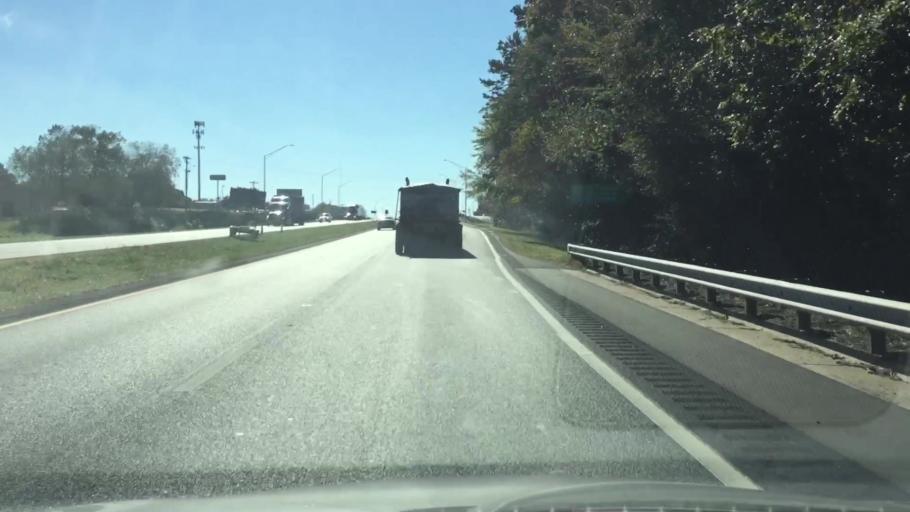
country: US
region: North Carolina
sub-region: Guilford County
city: Greensboro
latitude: 36.1239
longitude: -79.7494
